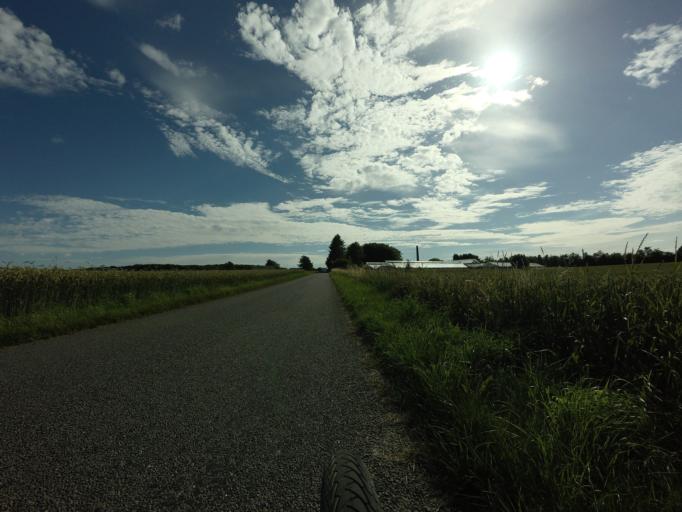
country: DK
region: Central Jutland
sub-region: Skanderborg Kommune
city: Horning
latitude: 56.0935
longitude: 10.0147
